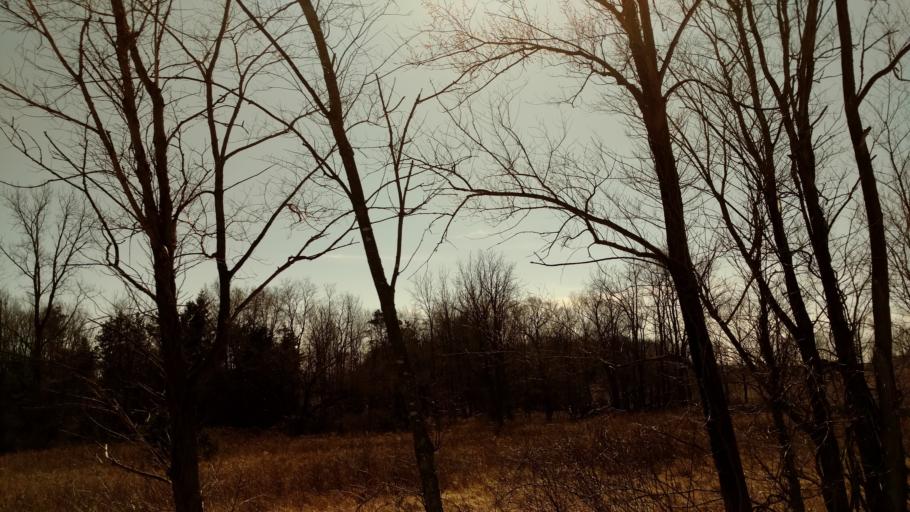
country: US
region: Ohio
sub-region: Union County
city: Richwood
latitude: 40.5121
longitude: -83.3527
